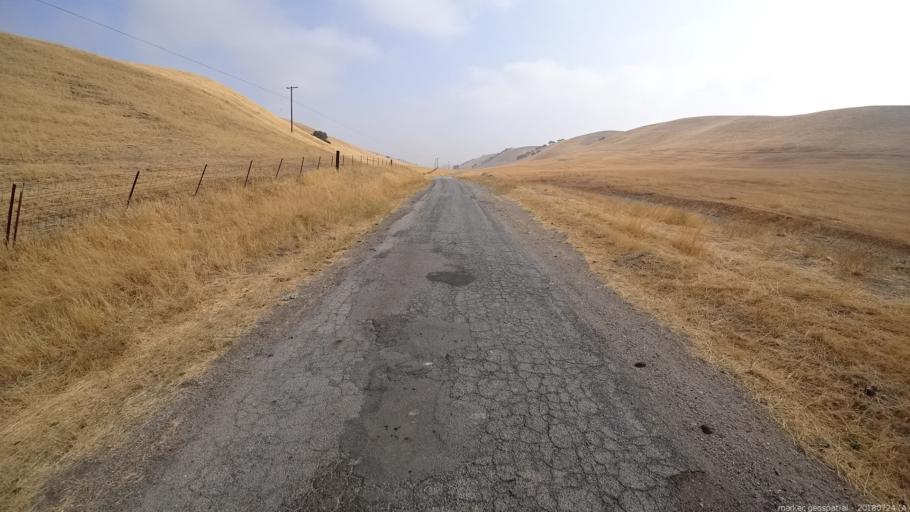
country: US
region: California
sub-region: San Luis Obispo County
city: San Miguel
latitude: 35.8721
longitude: -120.7933
